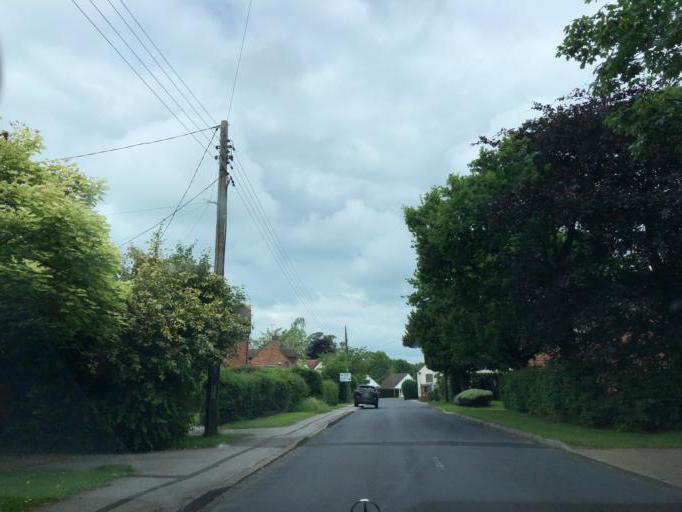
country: GB
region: England
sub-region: Solihull
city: Balsall Common
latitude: 52.3835
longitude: -1.6353
